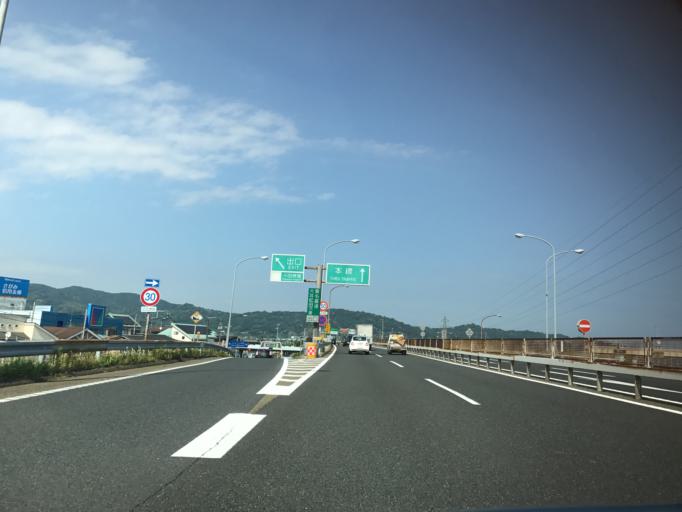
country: JP
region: Kanagawa
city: Odawara
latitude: 35.2855
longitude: 139.1684
